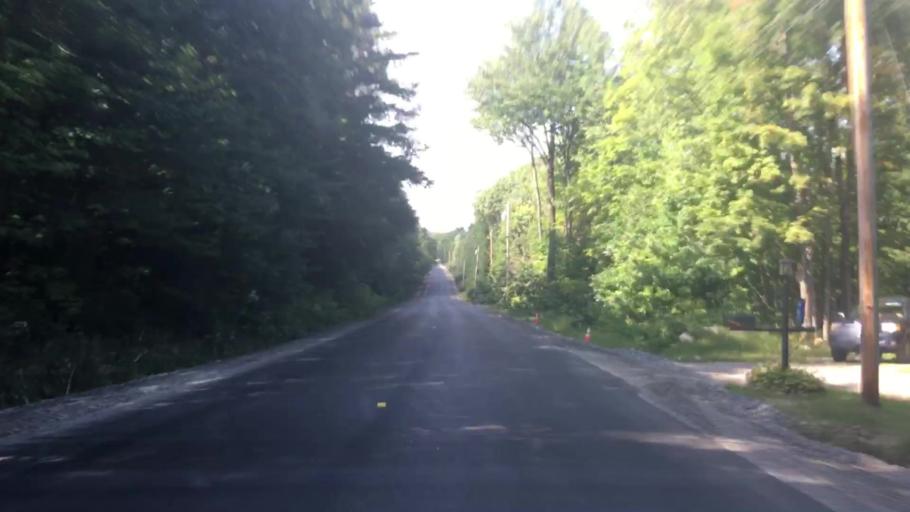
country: US
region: Maine
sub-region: Androscoggin County
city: Poland
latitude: 44.0254
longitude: -70.4280
